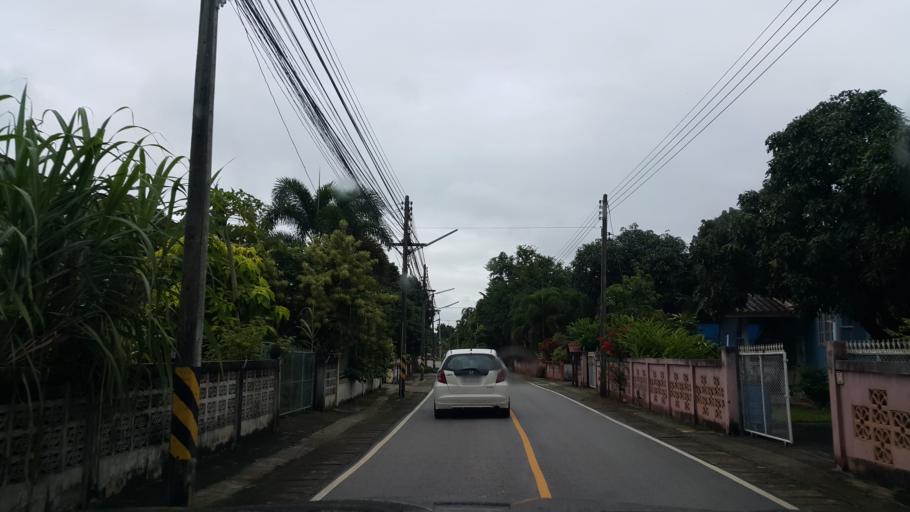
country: TH
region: Phayao
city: Chiang Kham
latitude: 19.5330
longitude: 100.2954
